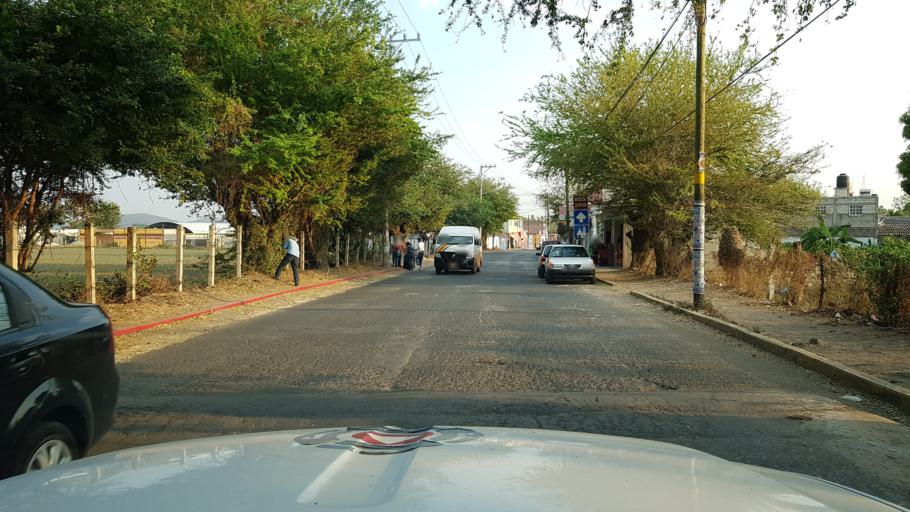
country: MX
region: Morelos
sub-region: Ayala
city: Ciudad Ayala
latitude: 18.7836
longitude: -98.9800
